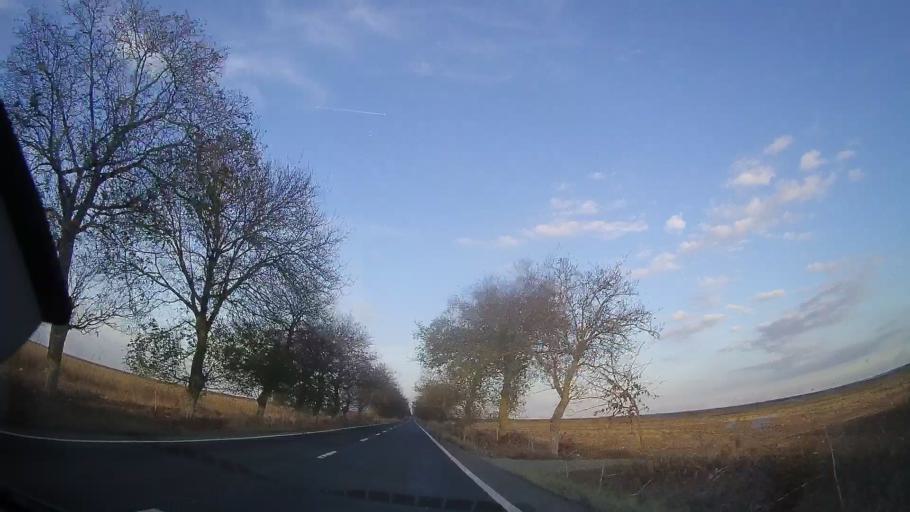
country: RO
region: Constanta
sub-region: Comuna Chirnogeni
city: Chirnogeni
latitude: 43.8508
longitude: 28.2422
